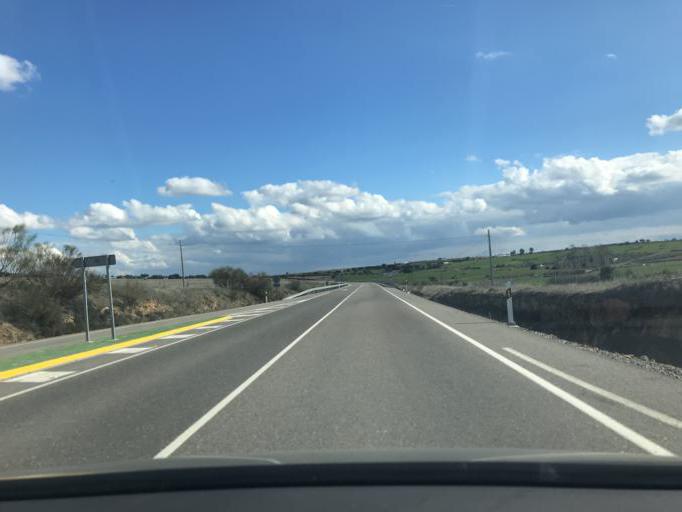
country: ES
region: Andalusia
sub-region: Province of Cordoba
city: Fuente Obejuna
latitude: 38.2685
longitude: -5.5053
